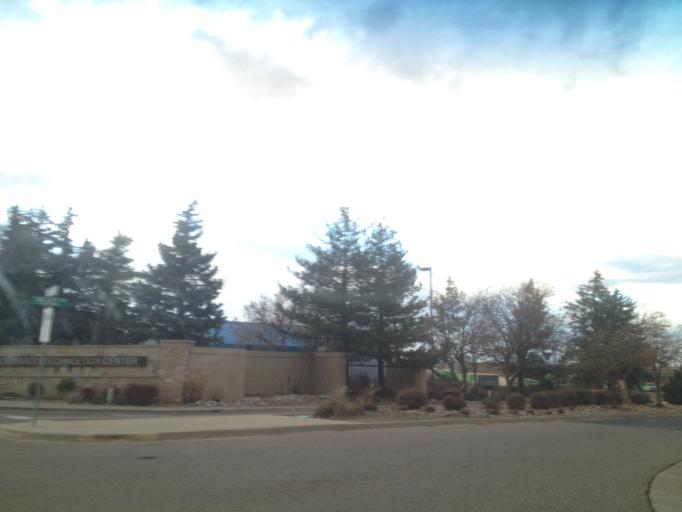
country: US
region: Colorado
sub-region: Boulder County
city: Louisville
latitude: 39.9580
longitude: -105.1214
